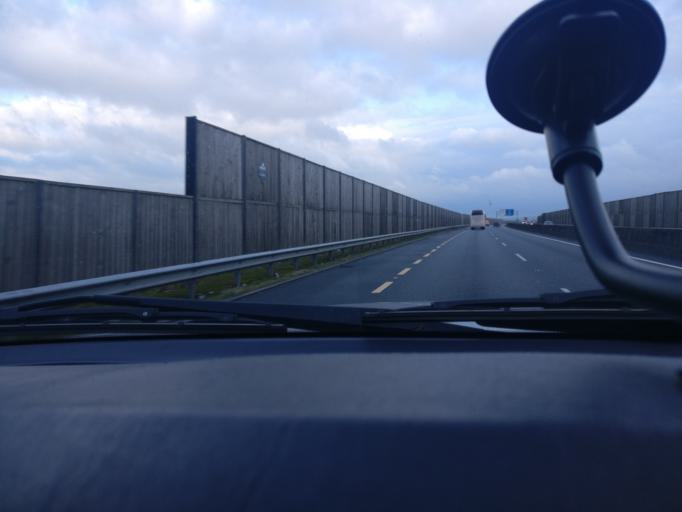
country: IE
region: Connaught
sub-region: County Galway
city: Oranmore
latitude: 53.2936
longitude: -8.9544
